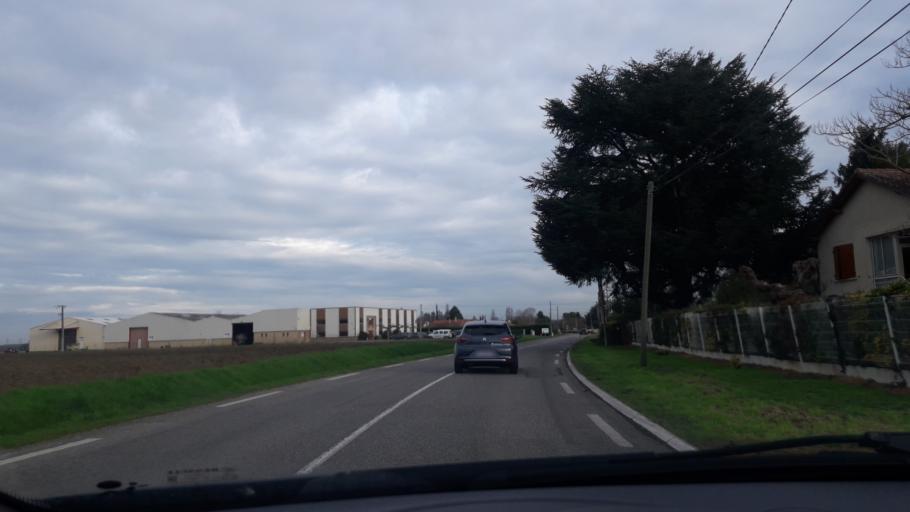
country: FR
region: Midi-Pyrenees
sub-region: Departement du Tarn-et-Garonne
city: Grisolles
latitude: 43.8144
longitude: 1.2903
